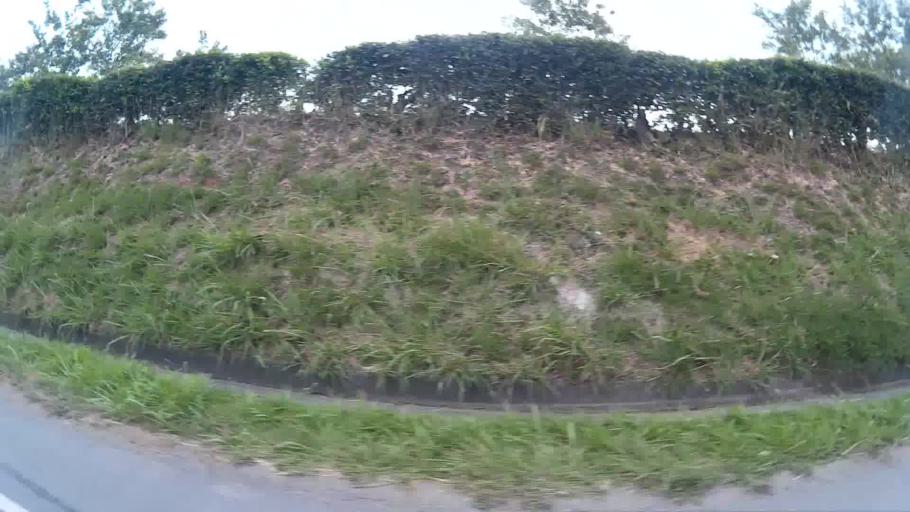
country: CO
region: Risaralda
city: La Virginia
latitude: 4.8654
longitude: -75.8688
